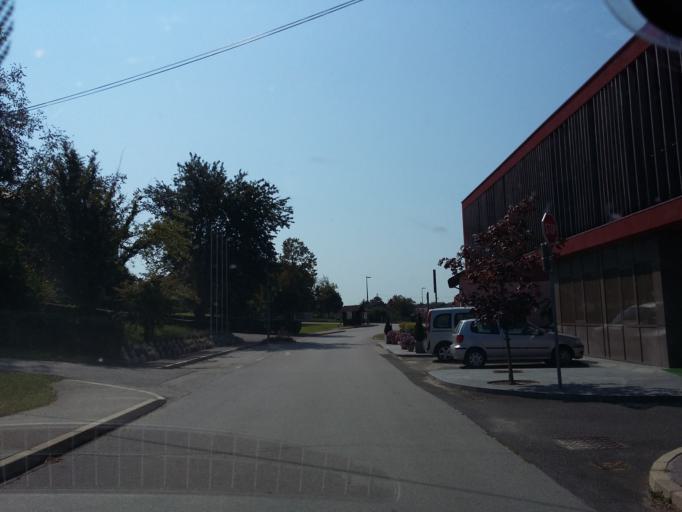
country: SI
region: Hodos-Hodos
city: Hodos
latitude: 46.8284
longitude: 16.3249
